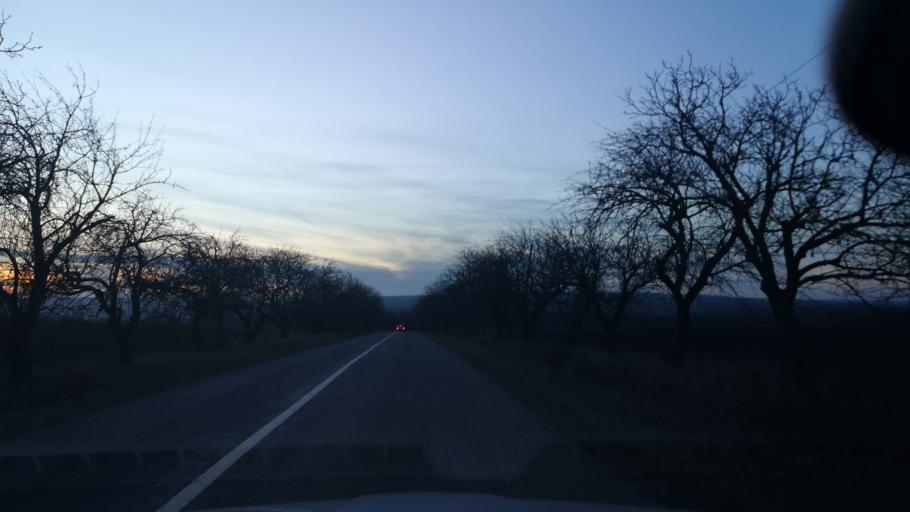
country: MD
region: Orhei
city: Orhei
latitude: 47.3117
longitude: 28.9480
